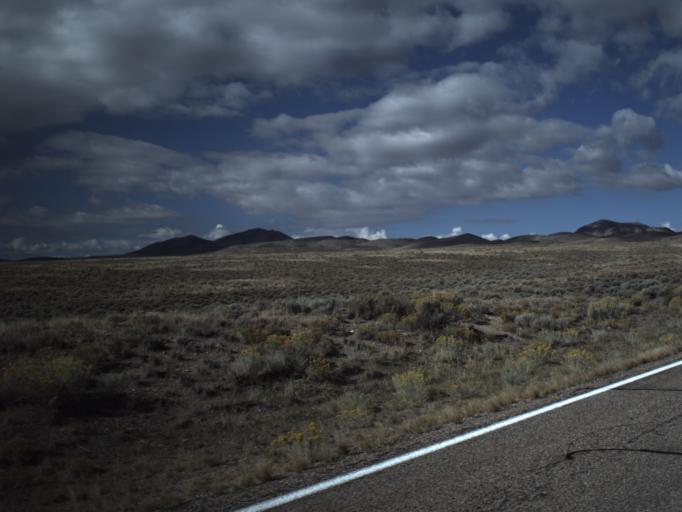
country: US
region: Utah
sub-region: Beaver County
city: Milford
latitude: 38.4475
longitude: -113.1883
